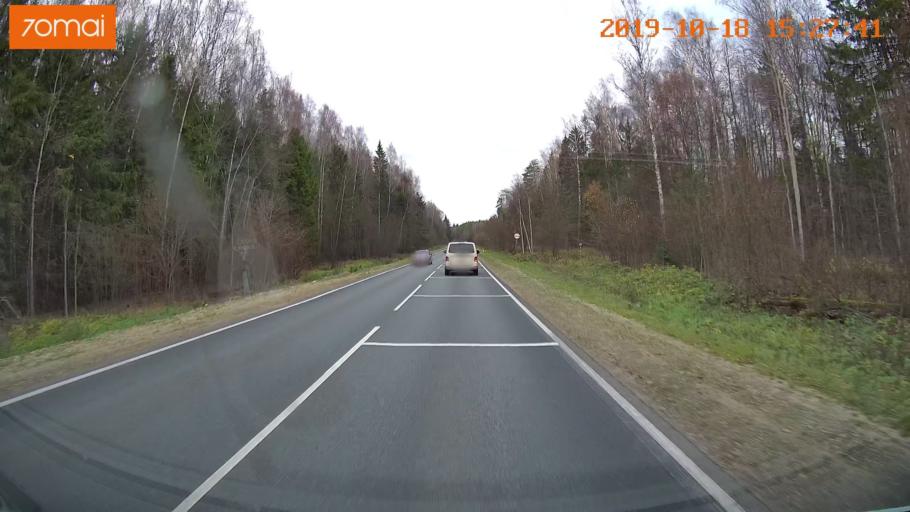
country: RU
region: Vladimir
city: Anopino
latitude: 55.7565
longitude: 40.6719
